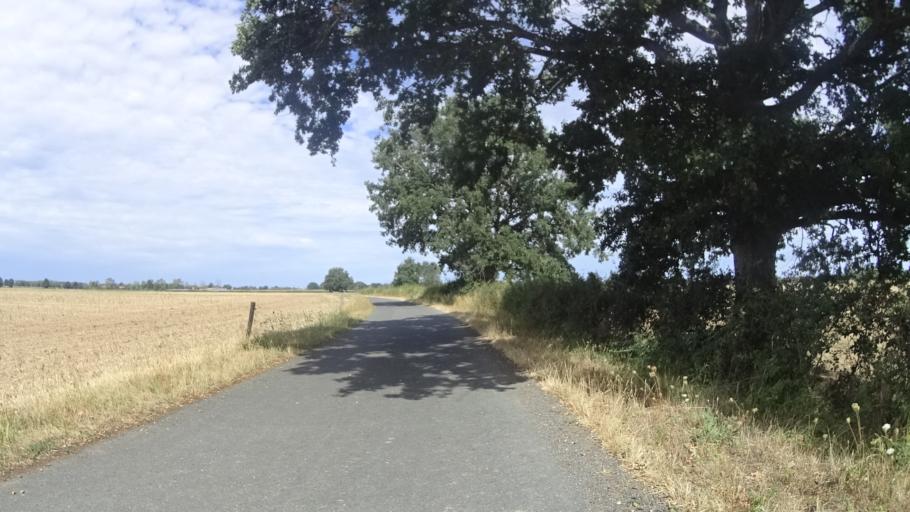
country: FR
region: Auvergne
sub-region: Departement de l'Allier
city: Beaulon
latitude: 46.6386
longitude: 3.6940
